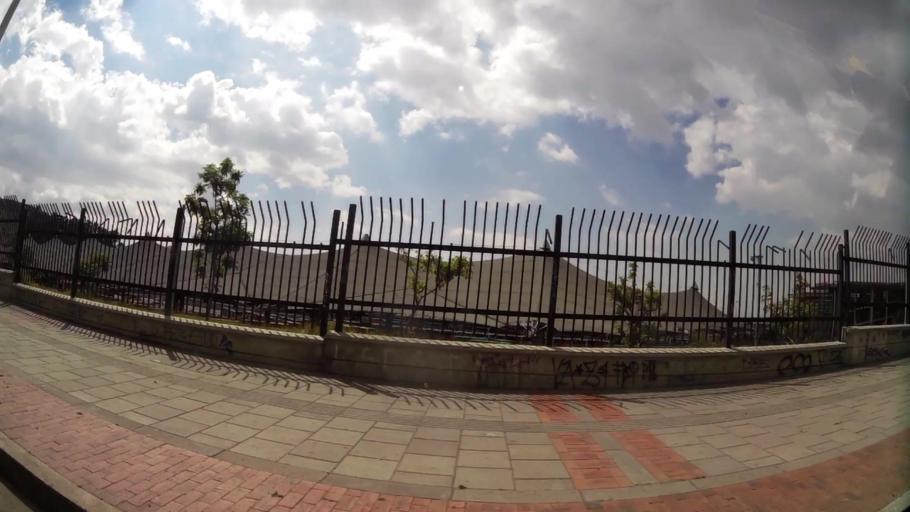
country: CO
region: Bogota D.C.
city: Bogota
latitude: 4.5650
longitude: -74.0949
